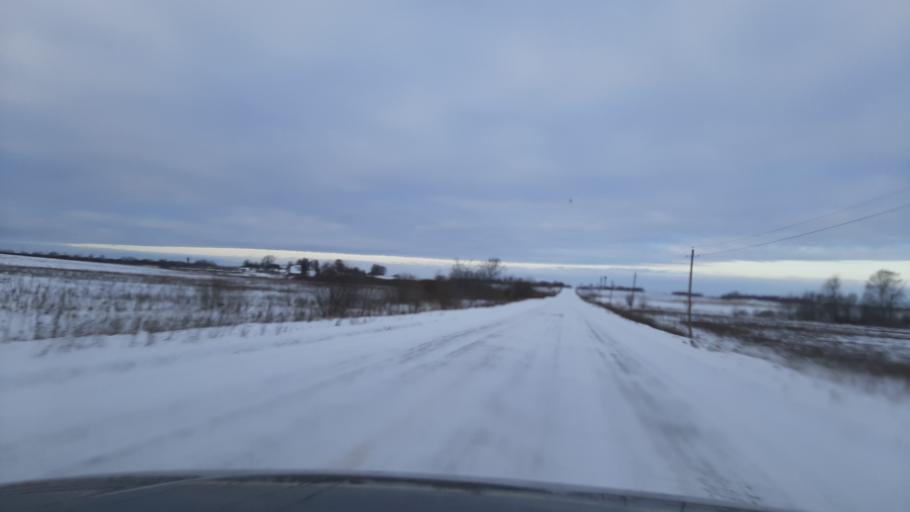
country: RU
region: Kostroma
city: Kosmynino
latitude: 57.4447
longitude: 40.9317
